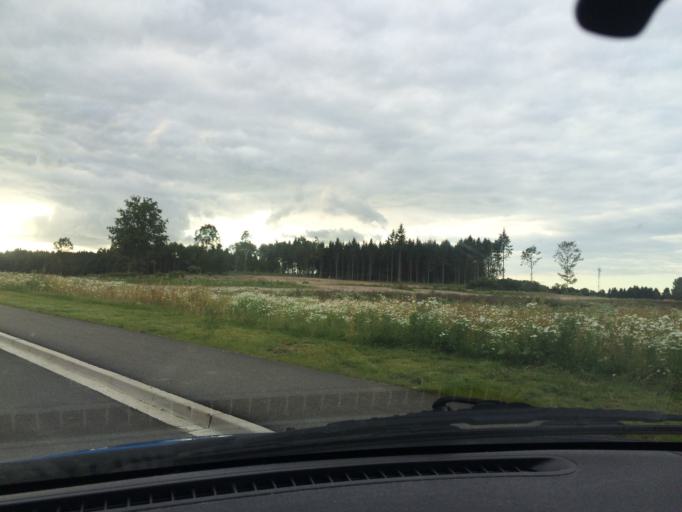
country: DE
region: Lower Saxony
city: Walsrode
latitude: 52.8461
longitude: 9.5593
